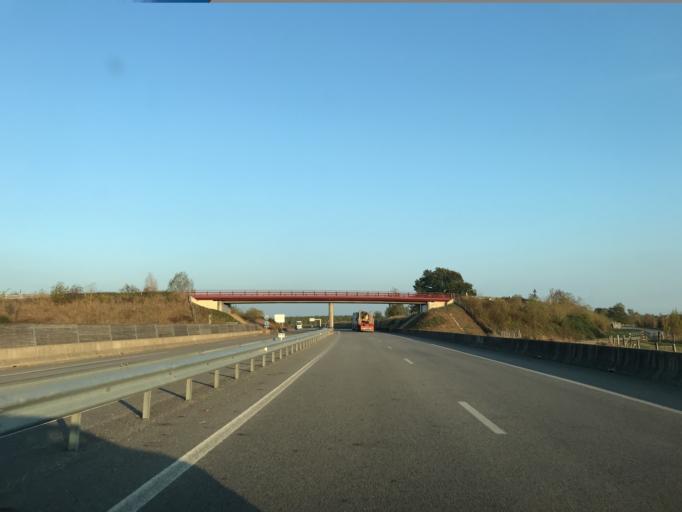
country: FR
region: Lower Normandy
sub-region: Departement de l'Orne
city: Valframbert
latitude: 48.4792
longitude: 0.2362
